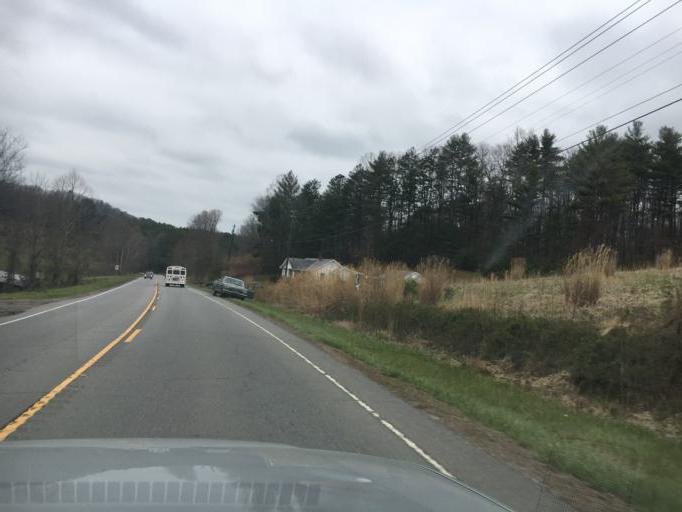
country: US
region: North Carolina
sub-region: Madison County
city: Mars Hill
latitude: 35.7705
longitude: -82.5132
